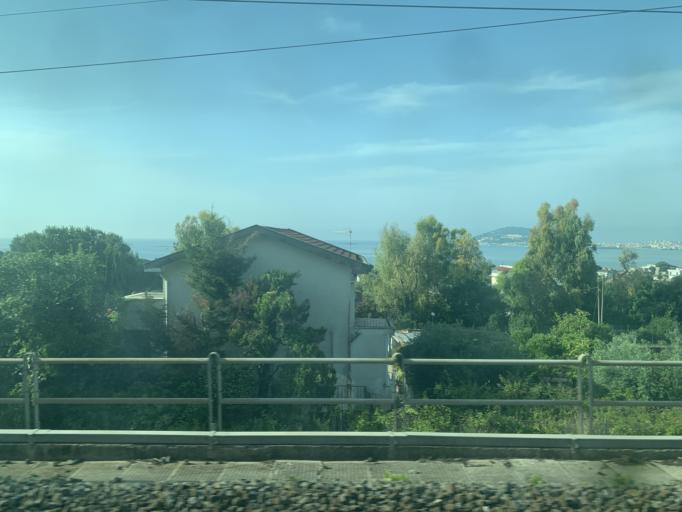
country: IT
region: Latium
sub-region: Provincia di Latina
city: Gaeta
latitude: 41.2544
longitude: 13.5873
